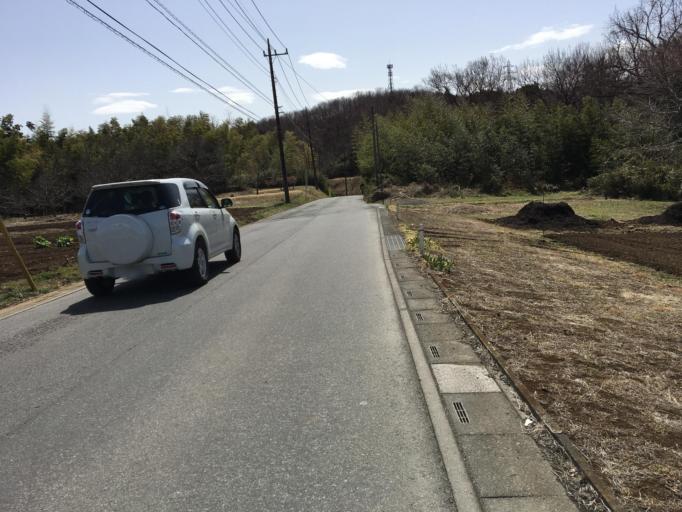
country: JP
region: Saitama
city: Ogawa
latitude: 36.0180
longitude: 139.3277
